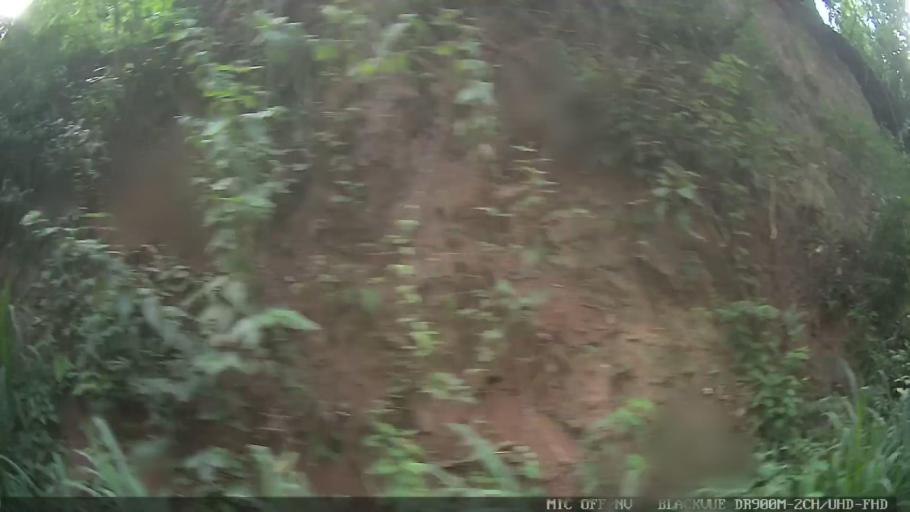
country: BR
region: Sao Paulo
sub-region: Braganca Paulista
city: Braganca Paulista
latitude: -22.9642
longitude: -46.6262
